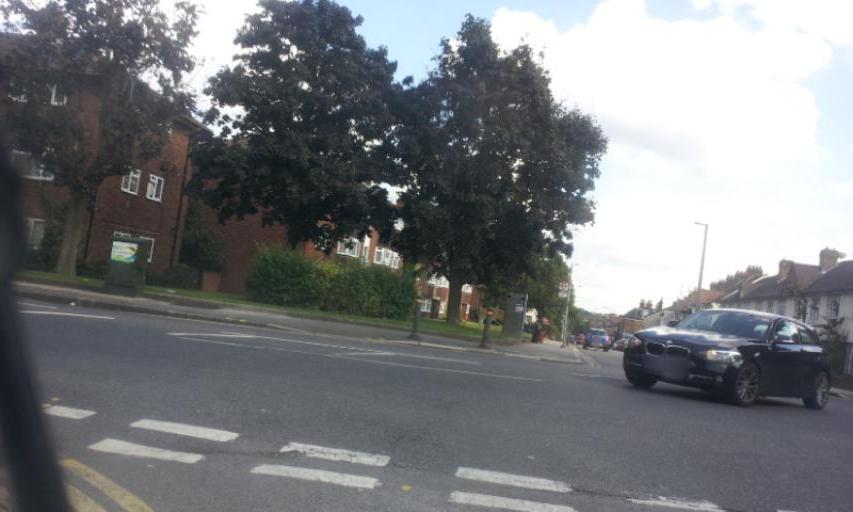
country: GB
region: England
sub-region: Greater London
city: Beckenham
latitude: 51.4196
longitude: -0.0534
